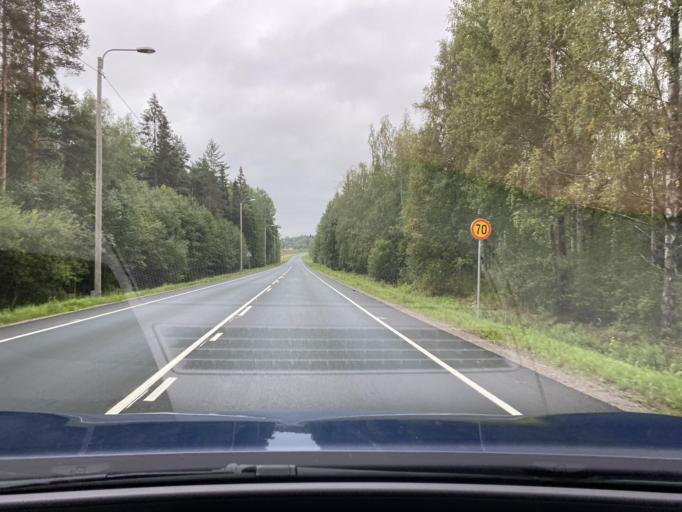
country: FI
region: Kymenlaakso
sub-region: Kouvola
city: Kouvola
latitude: 60.8932
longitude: 26.6042
